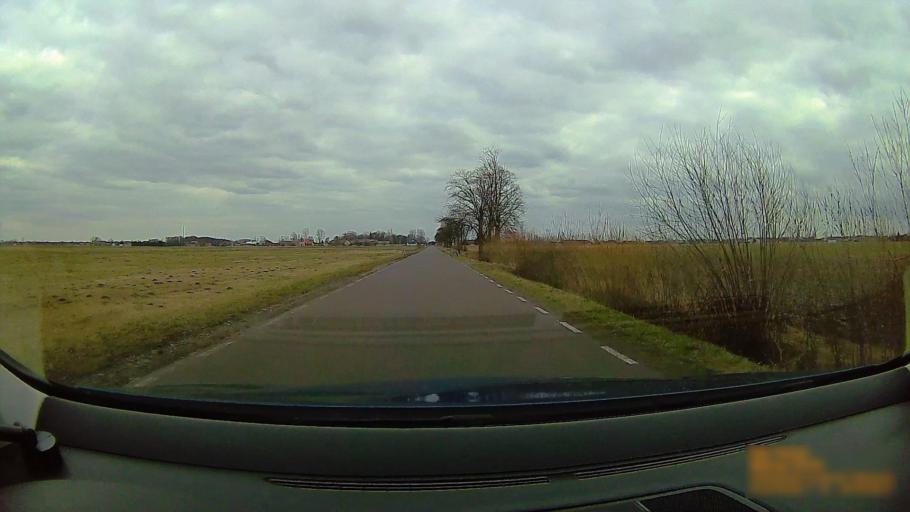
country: PL
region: Greater Poland Voivodeship
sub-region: Powiat koninski
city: Rychwal
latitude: 52.0968
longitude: 18.1300
